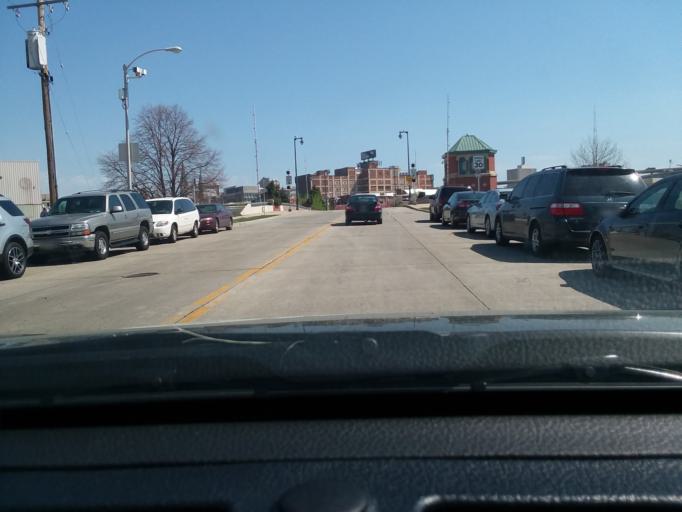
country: US
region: Wisconsin
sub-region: Milwaukee County
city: Milwaukee
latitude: 43.0317
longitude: -87.9299
